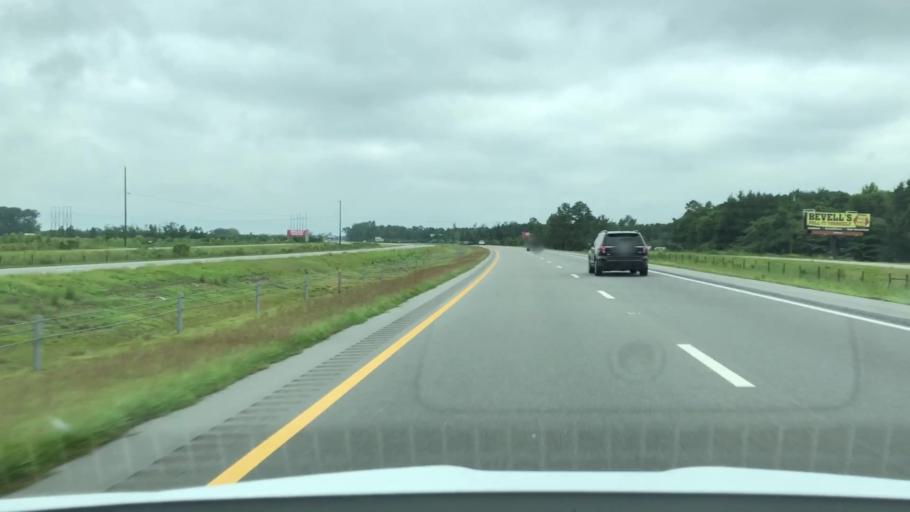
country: US
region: North Carolina
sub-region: Wayne County
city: Elroy
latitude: 35.3946
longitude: -77.8678
